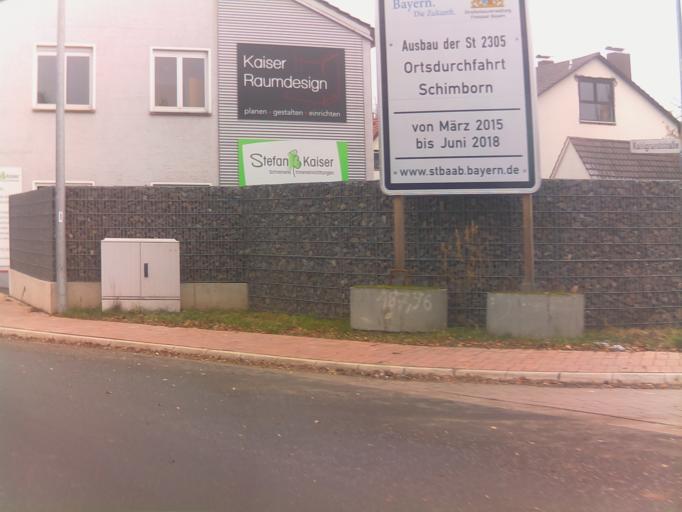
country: DE
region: Bavaria
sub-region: Regierungsbezirk Unterfranken
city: Mombris
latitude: 50.0545
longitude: 9.1916
